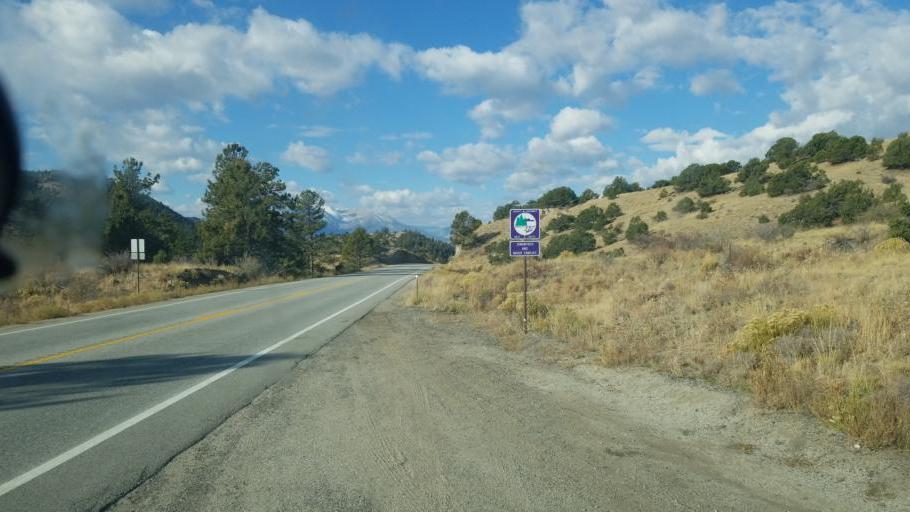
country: US
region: Colorado
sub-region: Chaffee County
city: Buena Vista
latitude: 38.8416
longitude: -105.9975
